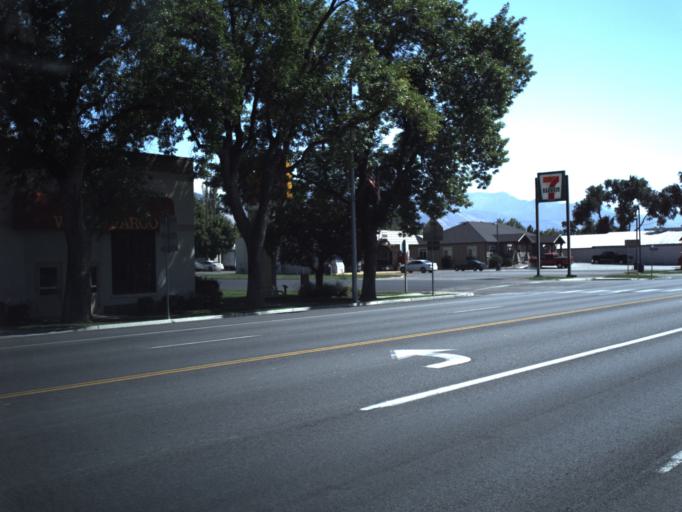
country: US
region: Utah
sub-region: Cache County
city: Smithfield
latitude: 41.8370
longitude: -111.8328
